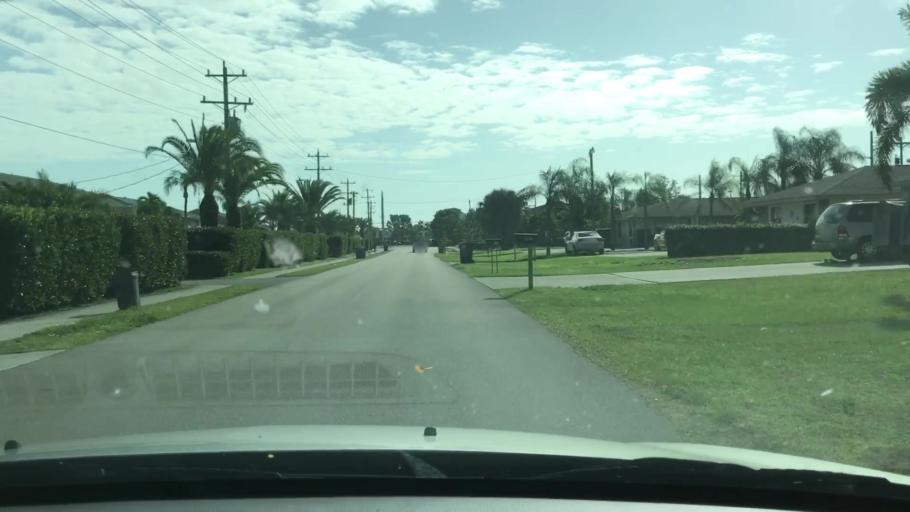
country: US
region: Florida
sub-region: Lee County
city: Lochmoor Waterway Estates
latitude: 26.6379
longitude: -81.9474
